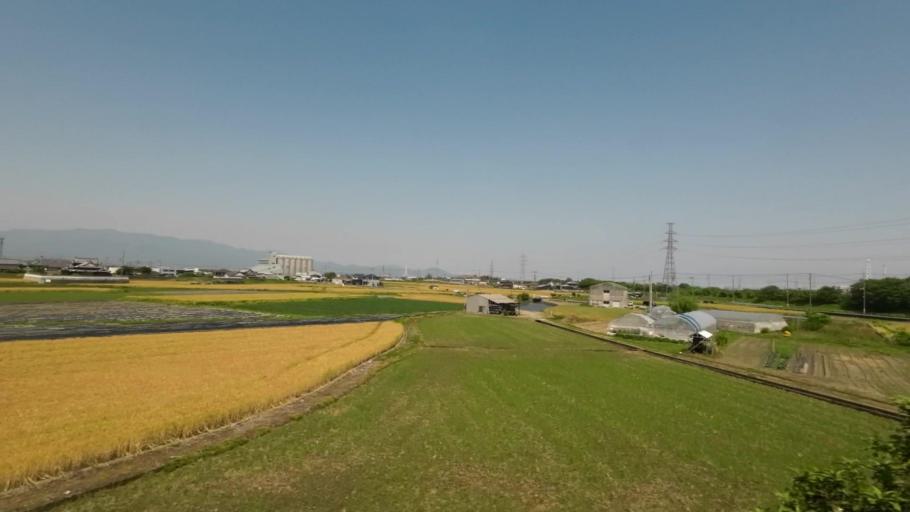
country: JP
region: Ehime
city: Saijo
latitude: 33.9038
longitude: 133.1778
